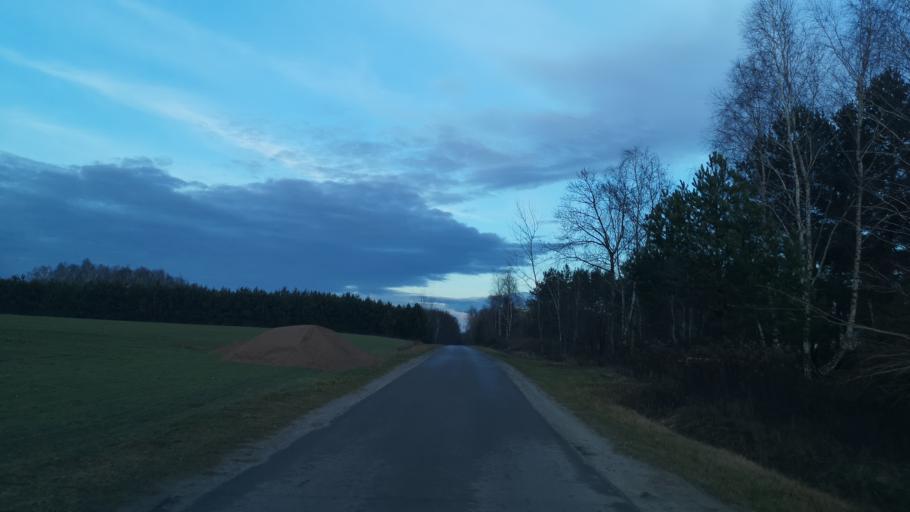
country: PL
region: Subcarpathian Voivodeship
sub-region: Powiat przeworski
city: Adamowka
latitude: 50.2551
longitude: 22.6396
